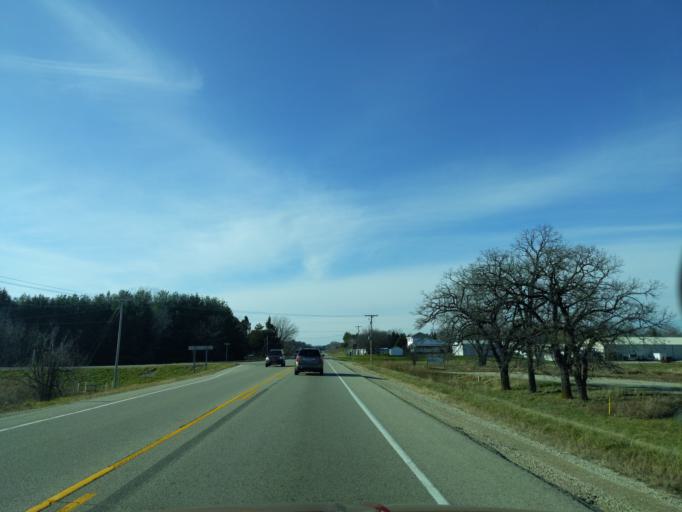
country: US
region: Wisconsin
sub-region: Rock County
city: Milton
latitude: 42.8247
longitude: -88.9831
